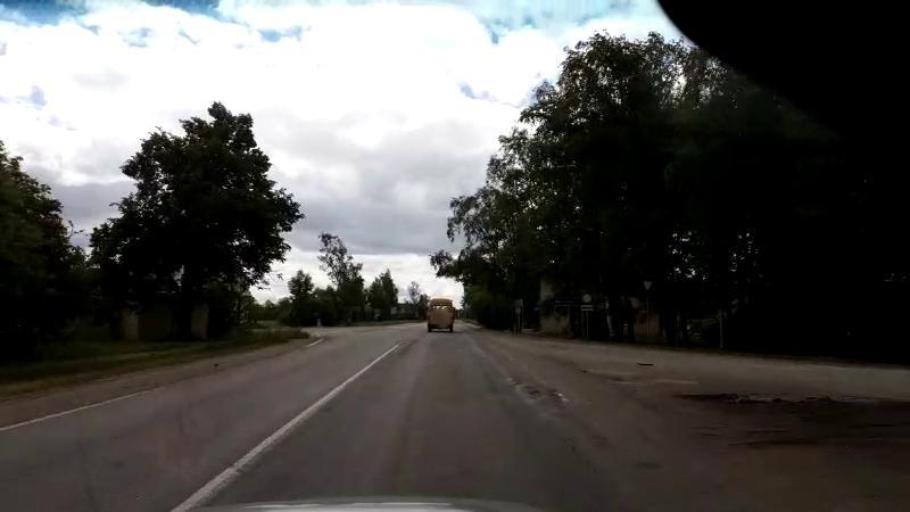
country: LV
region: Salacgrivas
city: Salacgriva
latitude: 57.7475
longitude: 24.3587
